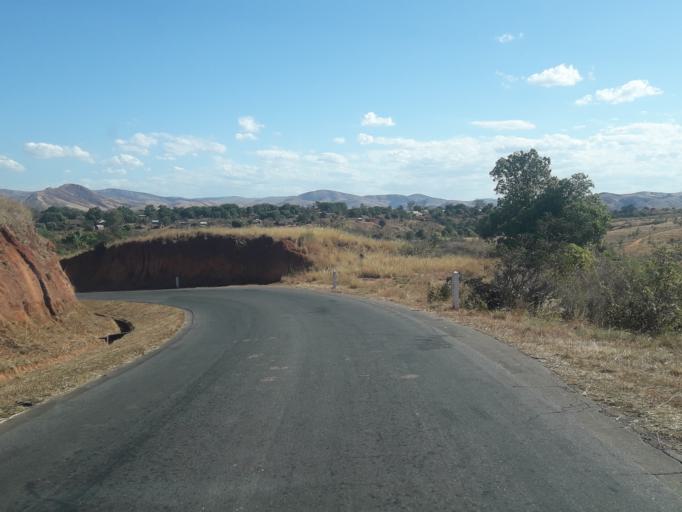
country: MG
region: Betsiboka
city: Maevatanana
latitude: -17.5913
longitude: 46.9353
